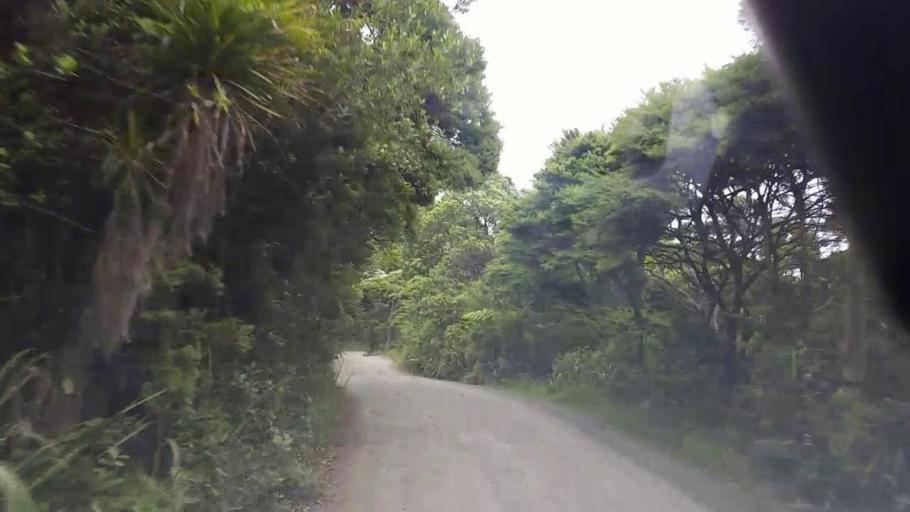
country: NZ
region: Auckland
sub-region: Auckland
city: Titirangi
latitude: -37.0314
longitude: 174.5199
